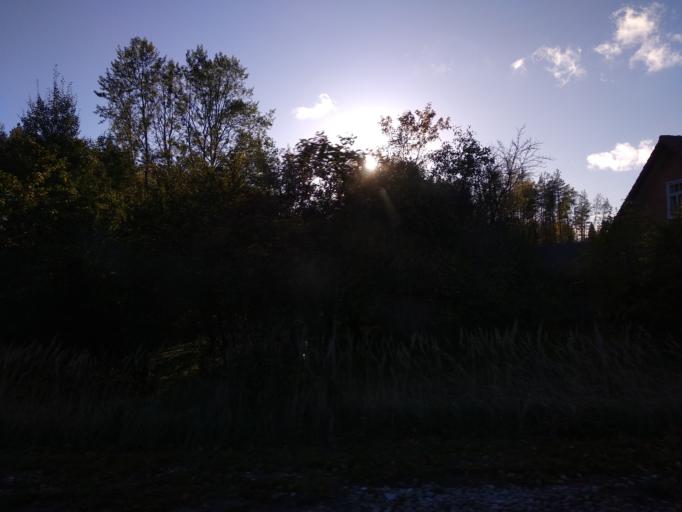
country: EE
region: Polvamaa
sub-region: Polva linn
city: Polva
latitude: 58.0492
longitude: 27.0633
